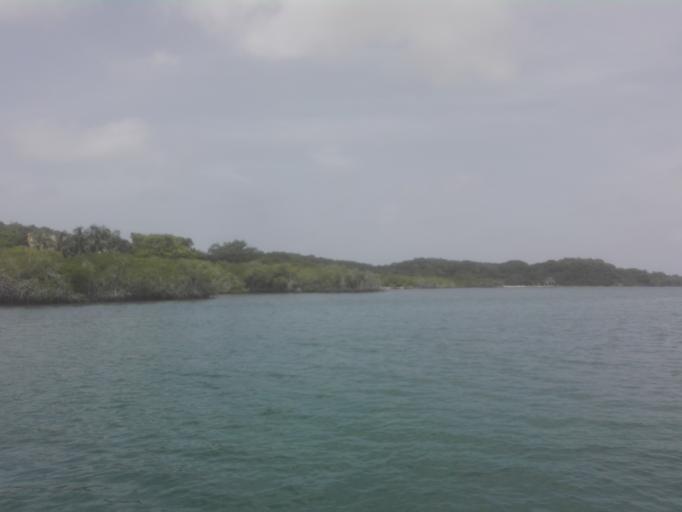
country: CO
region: Bolivar
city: Turbana
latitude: 10.1603
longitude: -75.6754
